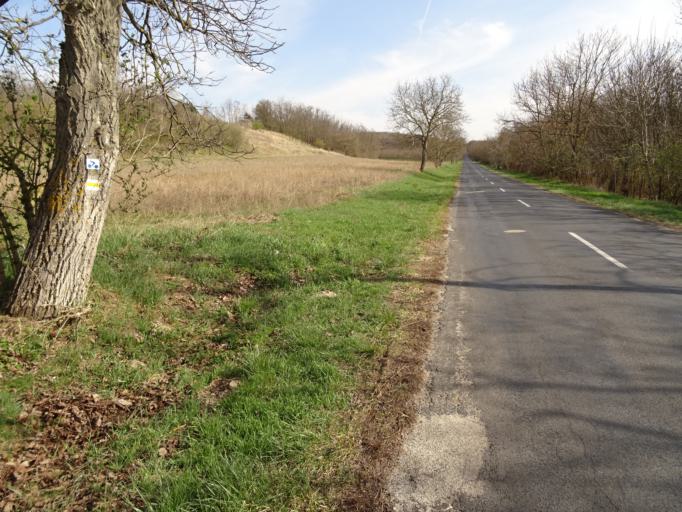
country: HU
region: Fejer
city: Lovasbereny
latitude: 47.2892
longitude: 18.5744
